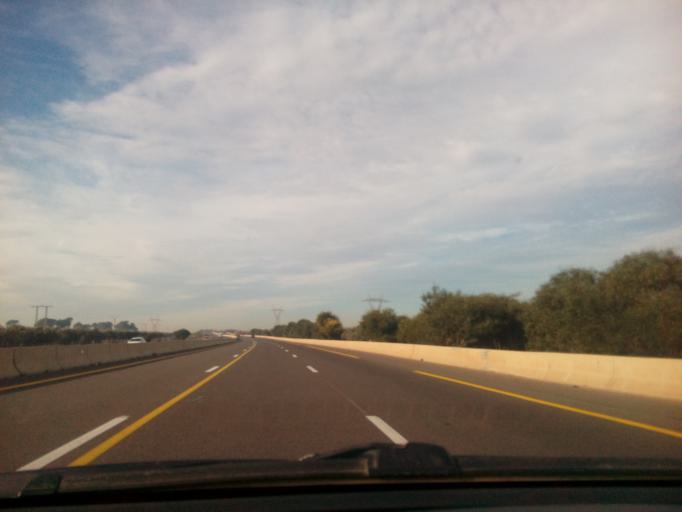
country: DZ
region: Mascara
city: Sig
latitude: 35.5799
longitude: -0.2519
